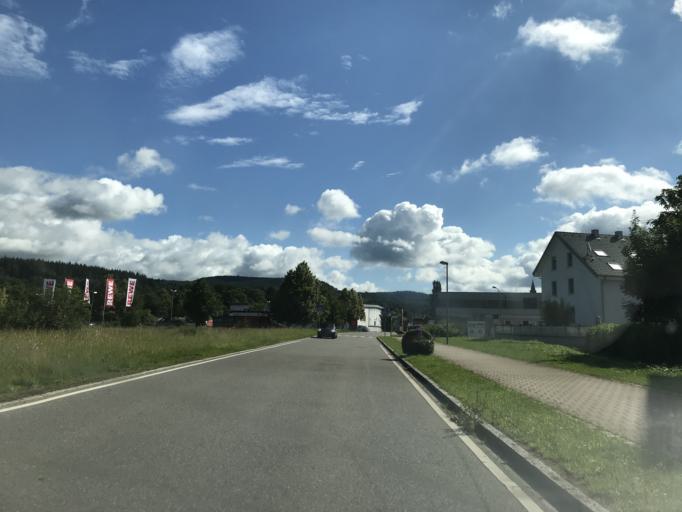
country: DE
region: Baden-Wuerttemberg
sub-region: Freiburg Region
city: Steinen
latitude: 47.6398
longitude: 7.7447
